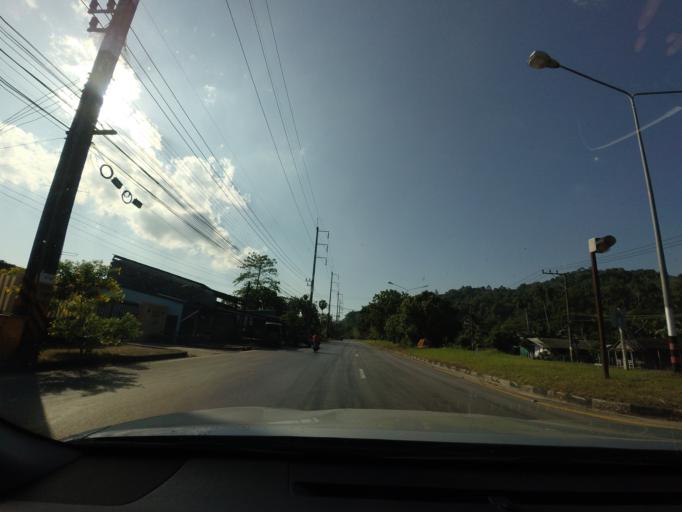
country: TH
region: Phangnga
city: Thai Mueang
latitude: 8.2717
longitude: 98.3277
